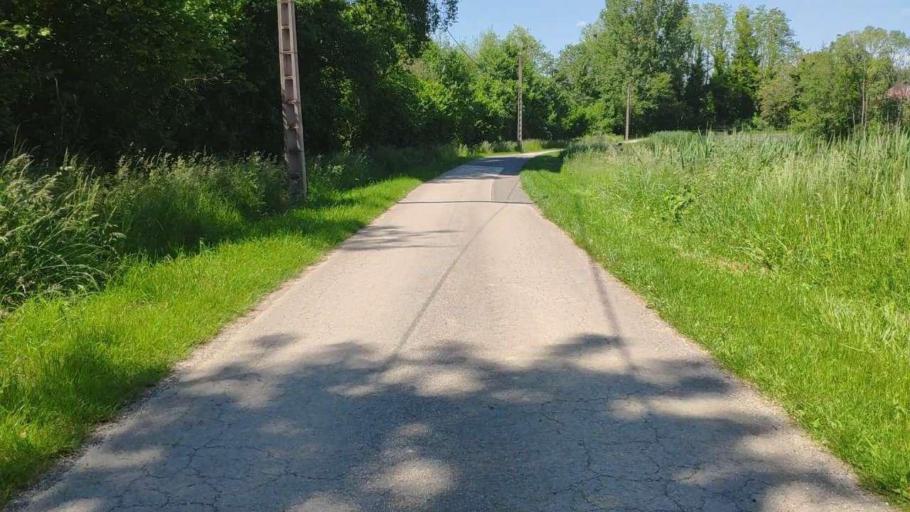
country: FR
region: Franche-Comte
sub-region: Departement du Jura
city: Bletterans
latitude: 46.7843
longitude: 5.3947
